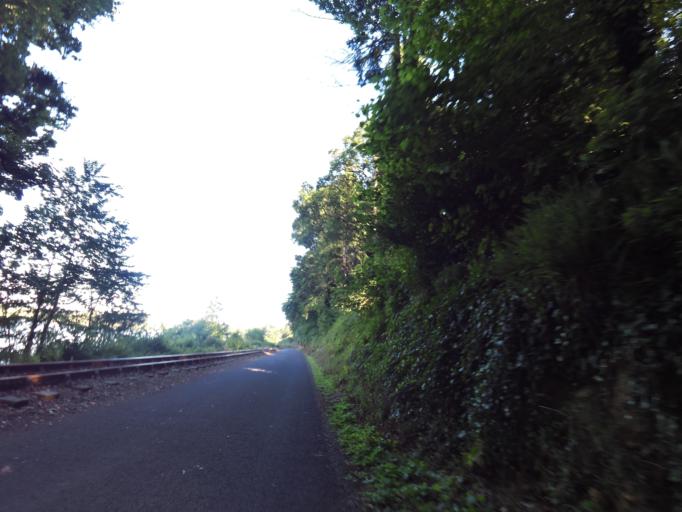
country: IE
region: Leinster
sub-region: Kilkenny
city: Mooncoin
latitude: 52.2450
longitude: -7.2267
